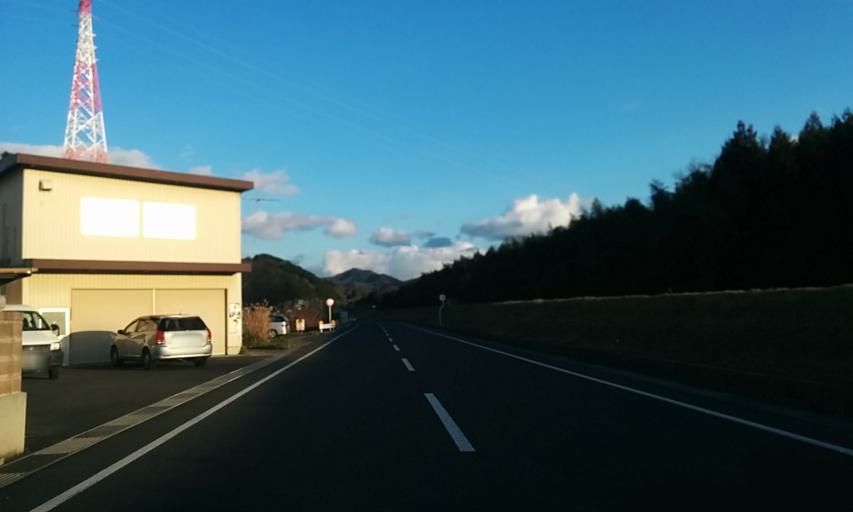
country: JP
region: Kyoto
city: Ayabe
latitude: 35.3123
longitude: 135.2549
